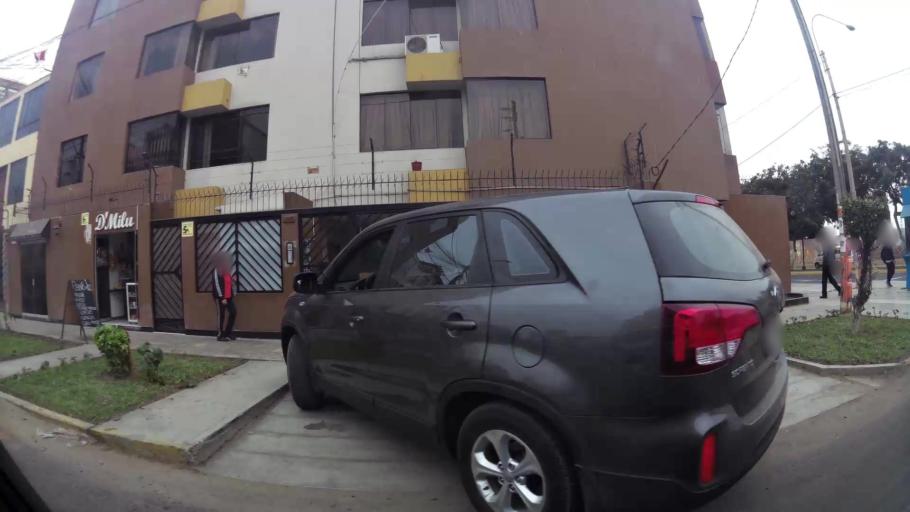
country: PE
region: La Libertad
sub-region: Provincia de Trujillo
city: Trujillo
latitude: -8.1182
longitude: -79.0389
